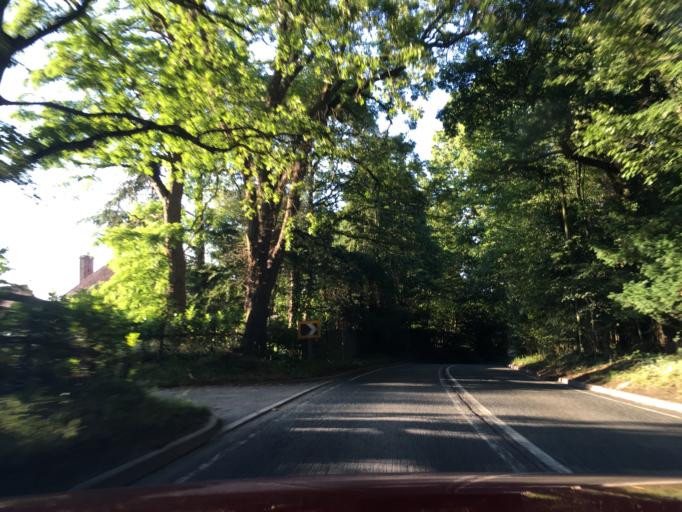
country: GB
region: England
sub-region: Hampshire
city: Tadley
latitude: 51.3739
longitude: -1.1514
